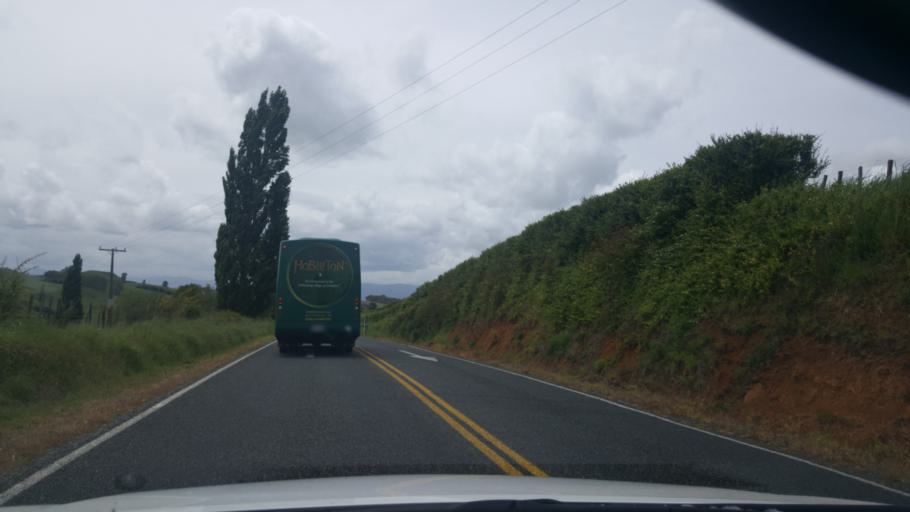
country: NZ
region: Waikato
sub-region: Matamata-Piako District
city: Matamata
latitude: -37.8796
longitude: 175.6979
